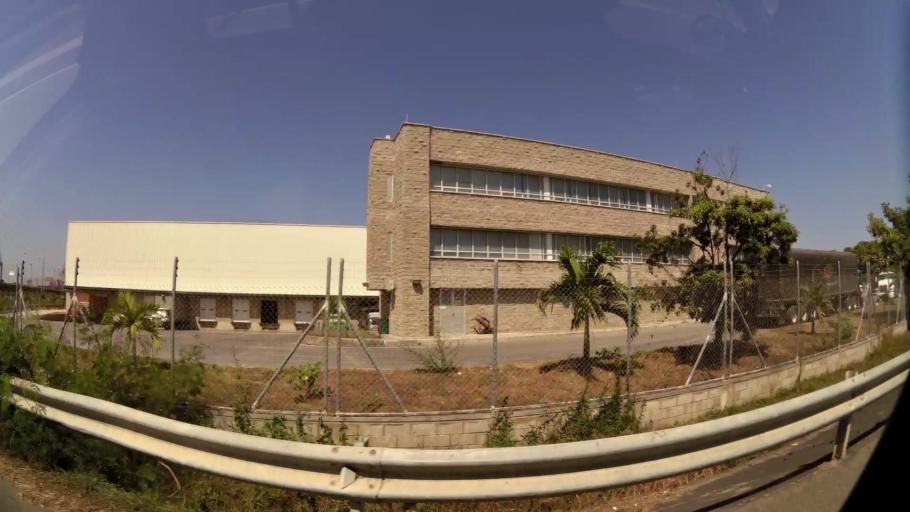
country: CO
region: Bolivar
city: Cartagena
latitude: 10.3805
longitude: -75.5023
